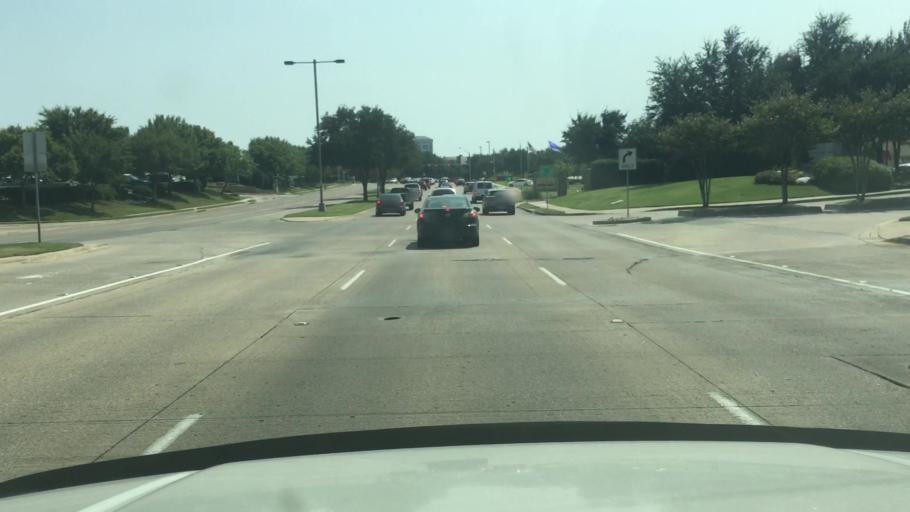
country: US
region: Texas
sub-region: Dallas County
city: Farmers Branch
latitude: 32.8983
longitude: -96.9589
